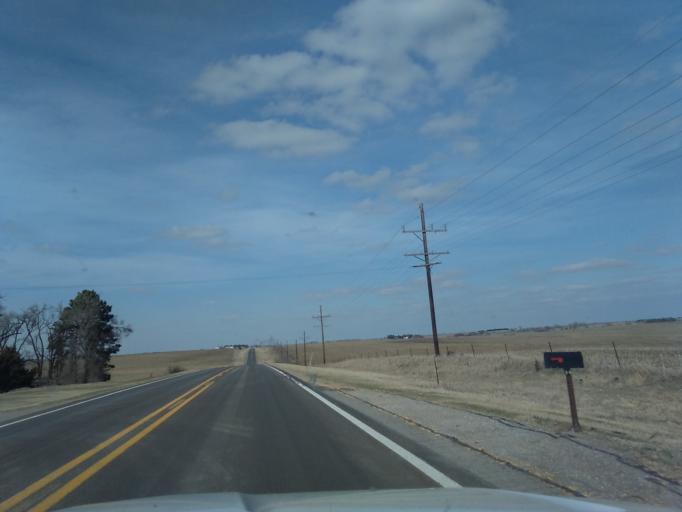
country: US
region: Nebraska
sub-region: Gage County
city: Beatrice
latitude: 40.1493
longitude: -96.9352
